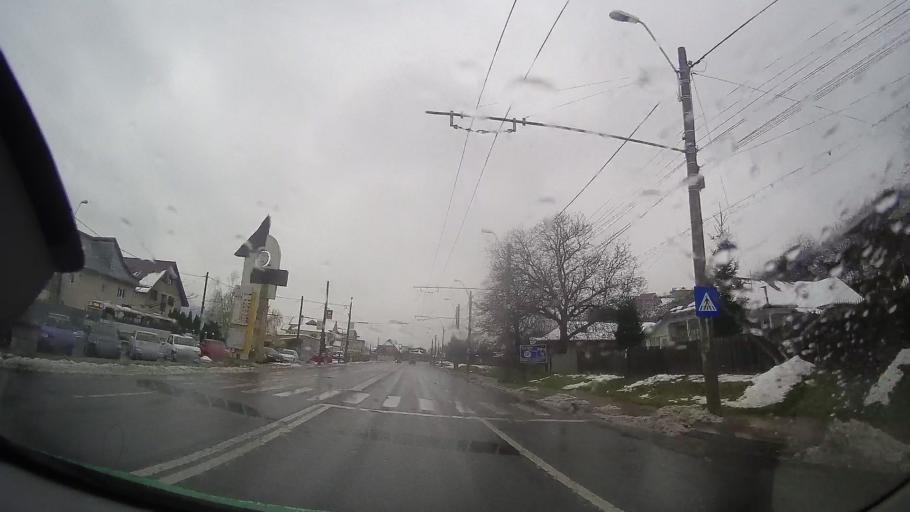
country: RO
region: Neamt
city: Piatra Neamt
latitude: 46.9405
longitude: 26.3260
